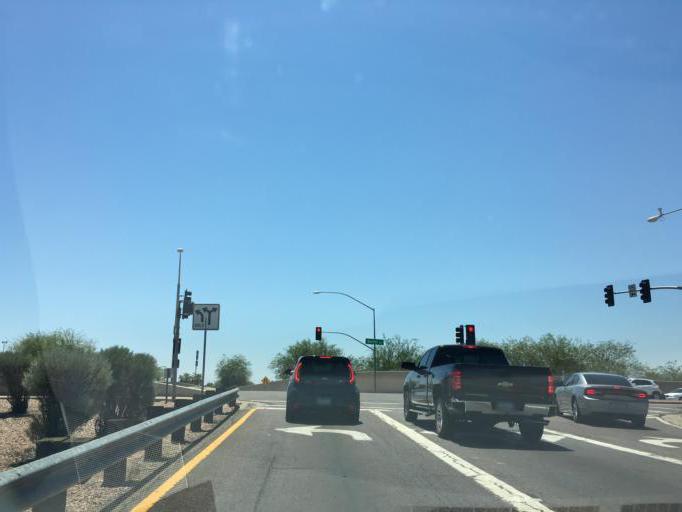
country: US
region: Arizona
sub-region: Maricopa County
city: Guadalupe
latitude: 33.3347
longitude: -111.9728
